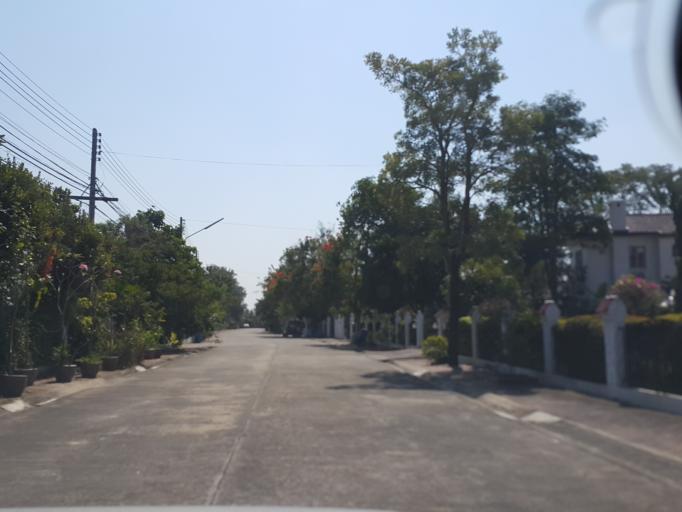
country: TH
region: Chiang Mai
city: Saraphi
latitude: 18.7575
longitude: 99.0256
